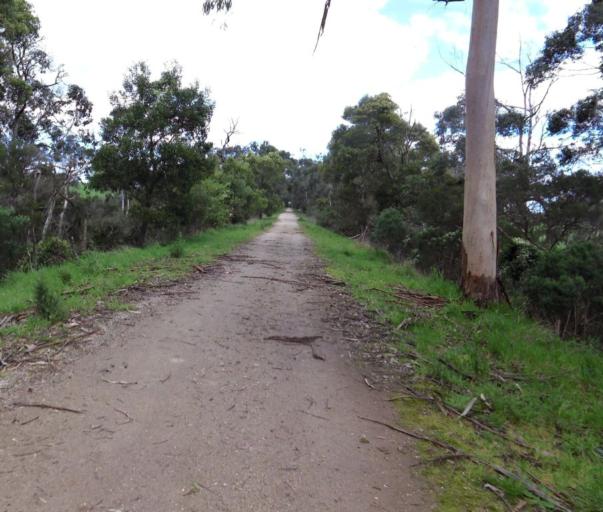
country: AU
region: Victoria
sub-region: Bass Coast
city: North Wonthaggi
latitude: -38.6605
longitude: 146.0254
